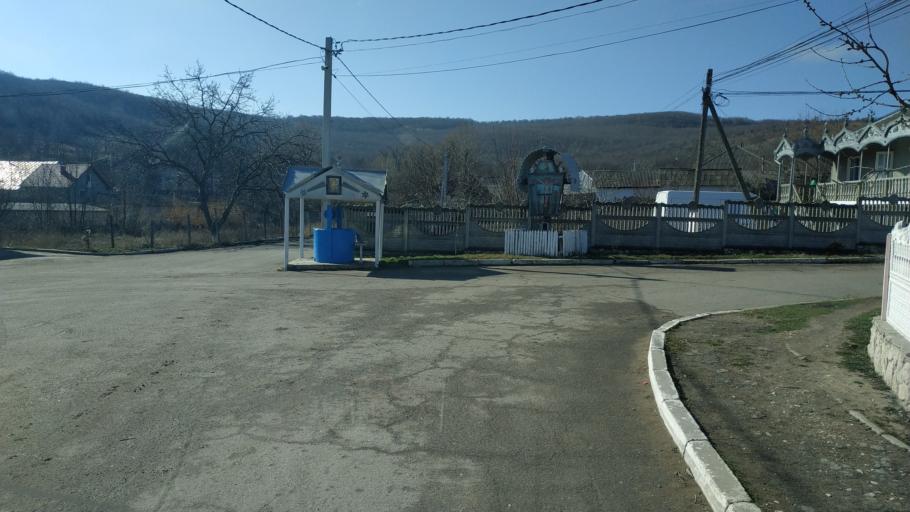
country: MD
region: Hincesti
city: Hincesti
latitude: 46.9197
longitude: 28.6255
